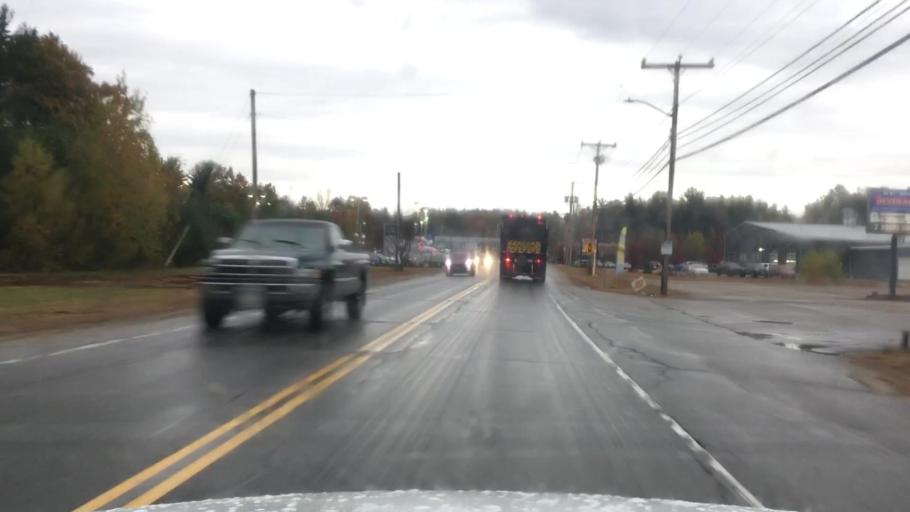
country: US
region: New Hampshire
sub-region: Strafford County
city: Somersworth
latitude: 43.2621
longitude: -70.9051
